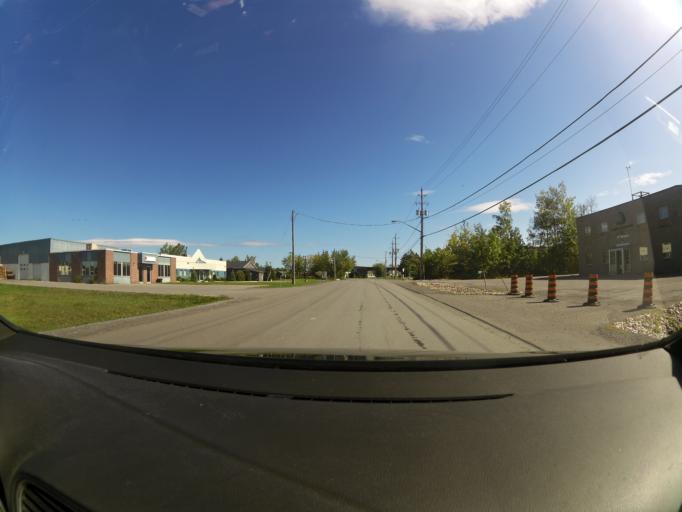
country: CA
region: Ontario
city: Bells Corners
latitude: 45.2717
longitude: -75.9562
